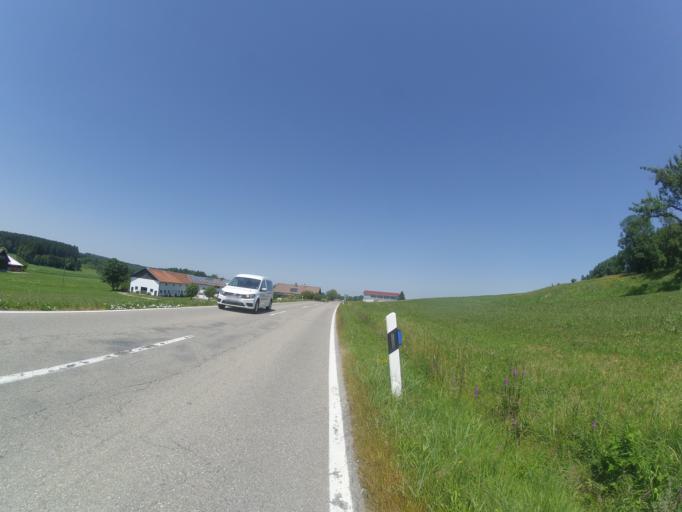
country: DE
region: Bavaria
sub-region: Swabia
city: Bohen
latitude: 47.8848
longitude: 10.3292
